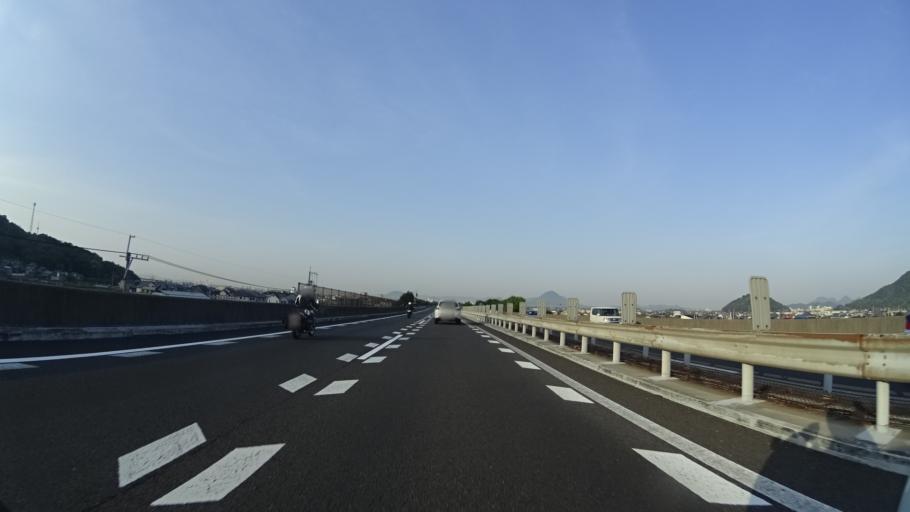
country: JP
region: Kagawa
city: Tadotsu
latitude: 34.2317
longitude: 133.7471
